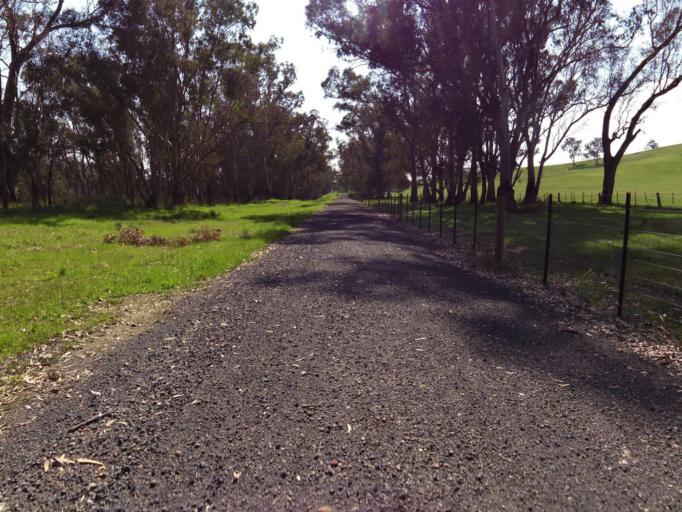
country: AU
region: Victoria
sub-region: Murrindindi
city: Alexandra
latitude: -37.1401
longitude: 145.5901
